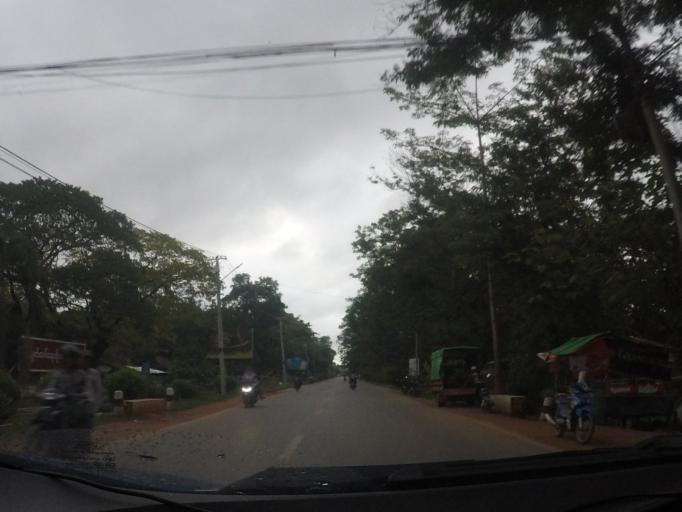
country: MM
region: Bago
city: Paungde
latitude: 18.3309
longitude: 95.6254
